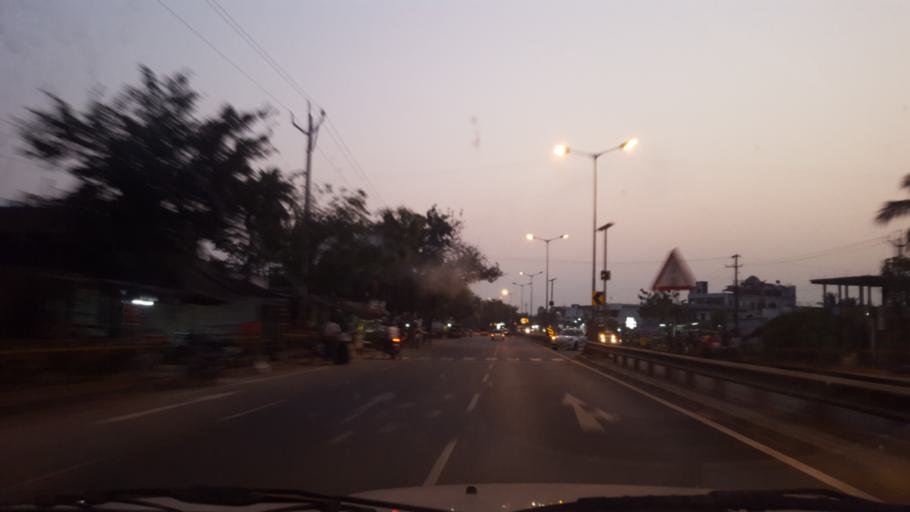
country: IN
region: Andhra Pradesh
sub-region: East Godavari
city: Peddapuram
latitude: 17.1573
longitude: 81.9912
